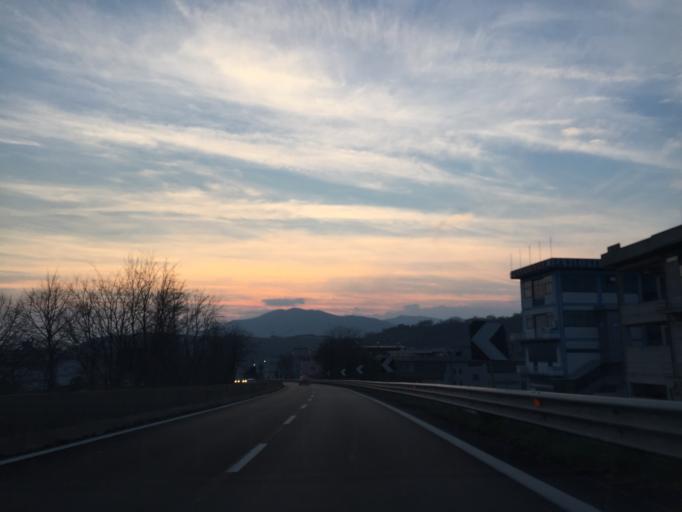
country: IT
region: Campania
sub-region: Provincia di Avellino
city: Solofra
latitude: 40.8340
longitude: 14.8273
